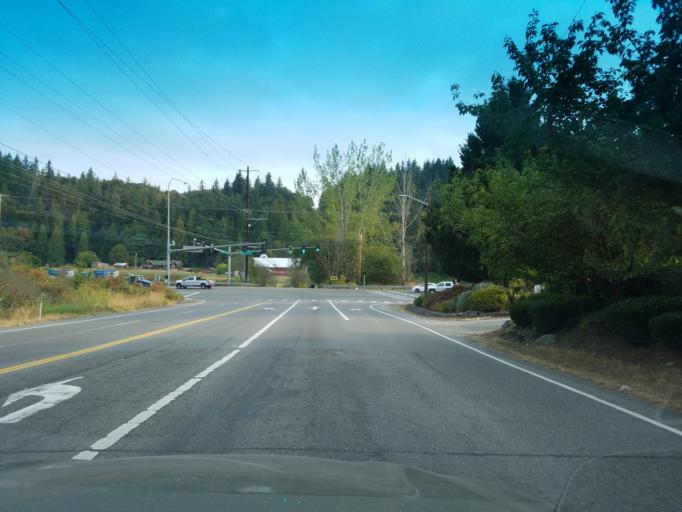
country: US
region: Washington
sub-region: King County
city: Sammamish
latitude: 47.6557
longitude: -122.0626
